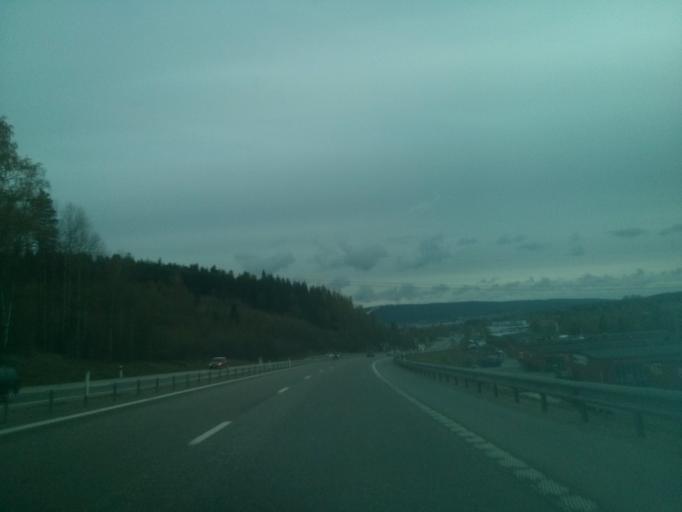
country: SE
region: Vaesternorrland
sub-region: Sundsvalls Kommun
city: Johannedal
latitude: 62.4233
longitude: 17.3491
